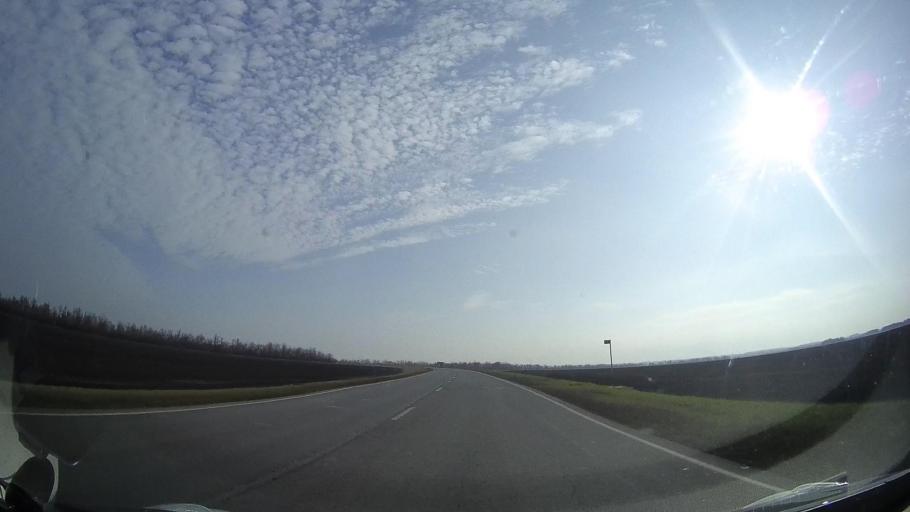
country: RU
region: Rostov
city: Tselina
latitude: 46.5137
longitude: 40.9997
